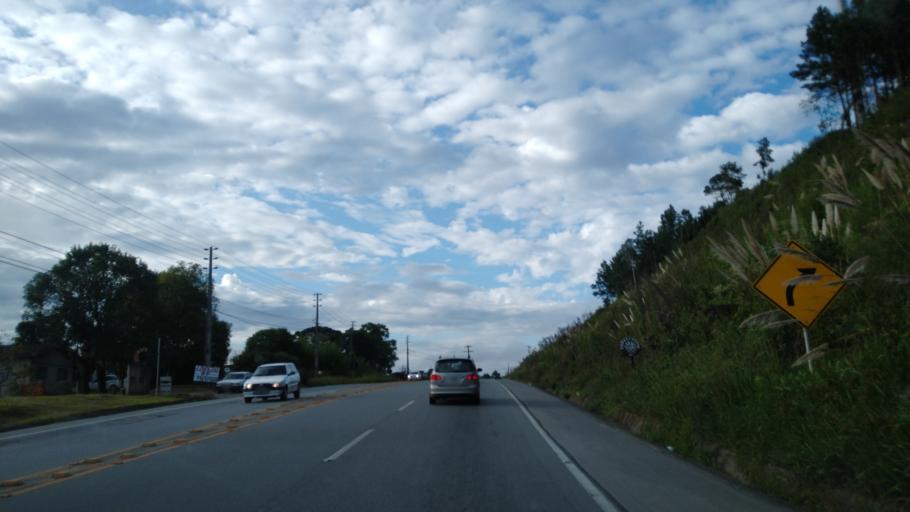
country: BR
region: Santa Catarina
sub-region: Sao Bento Do Sul
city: Sao Bento do Sul
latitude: -26.2334
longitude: -49.4260
